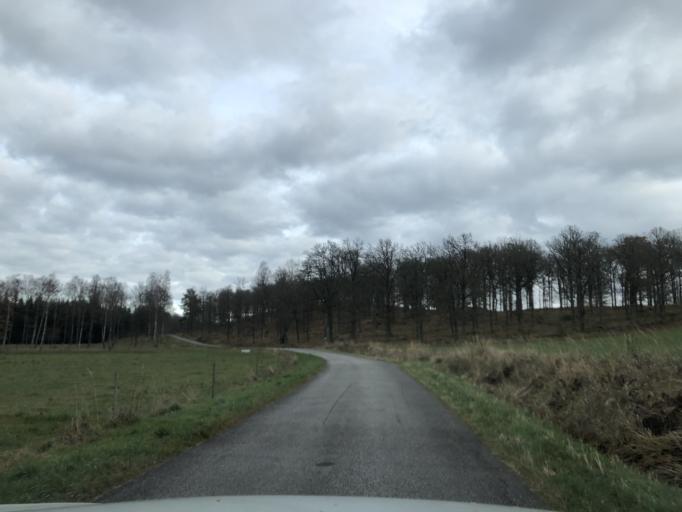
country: SE
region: Vaestra Goetaland
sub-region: Ulricehamns Kommun
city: Ulricehamn
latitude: 57.7110
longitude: 13.3522
